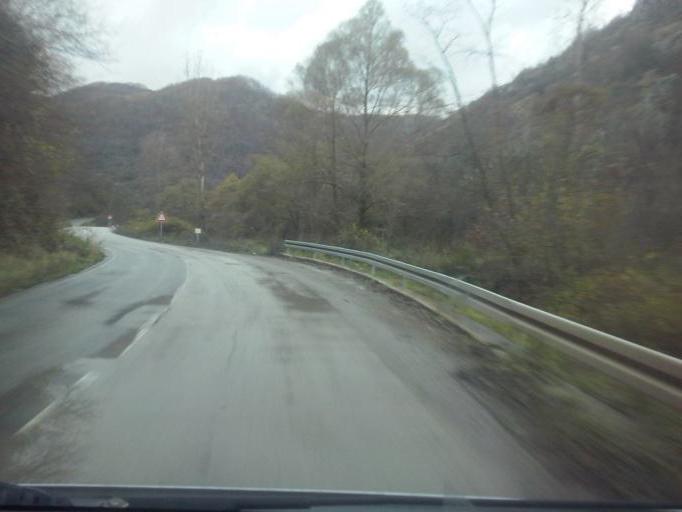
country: RS
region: Central Serbia
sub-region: Pirotski Okrug
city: Bela Palanka
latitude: 43.0310
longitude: 22.3970
